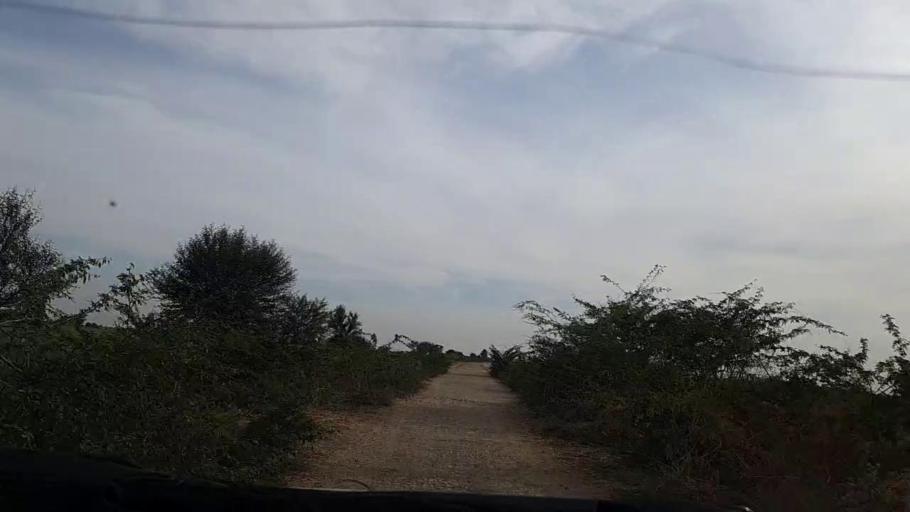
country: PK
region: Sindh
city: Dhoro Naro
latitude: 25.4003
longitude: 69.5176
